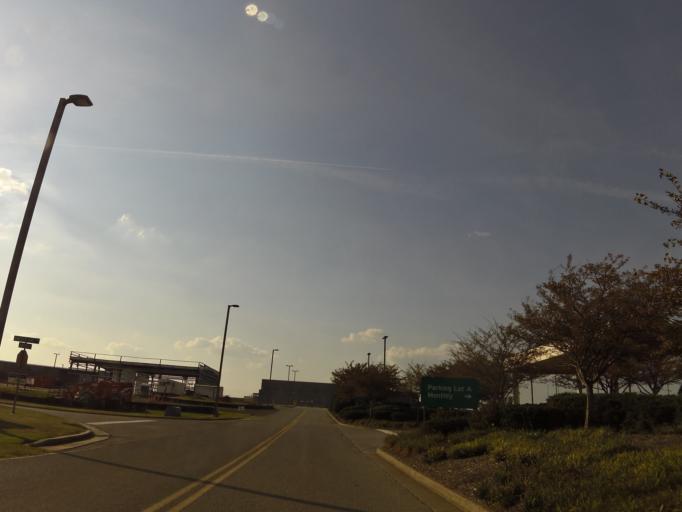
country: US
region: Tennessee
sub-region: Blount County
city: Alcoa
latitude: 35.8034
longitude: -83.9933
